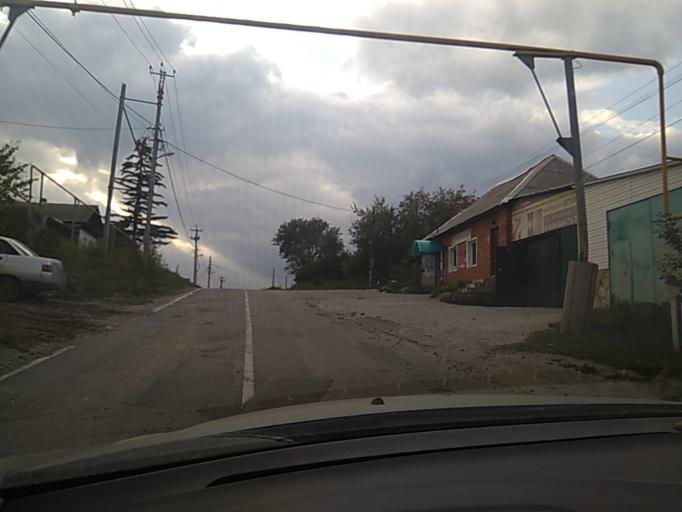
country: RU
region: Chelyabinsk
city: Kyshtym
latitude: 55.6978
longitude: 60.5410
